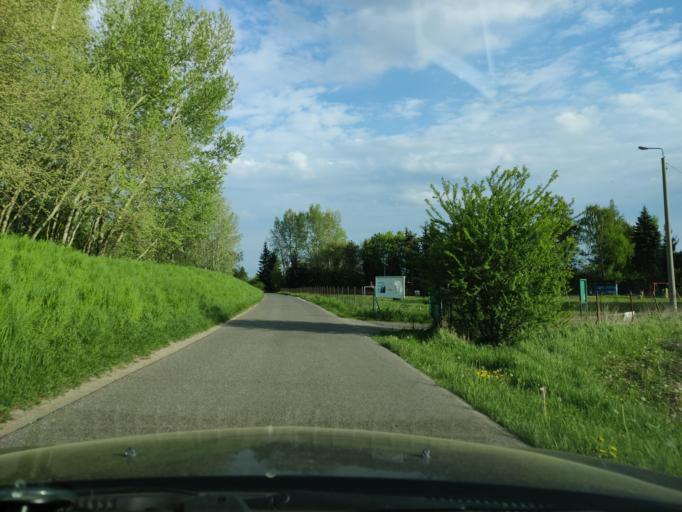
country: PL
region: Masovian Voivodeship
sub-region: Powiat otwocki
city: Jozefow
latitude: 52.1124
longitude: 21.1835
